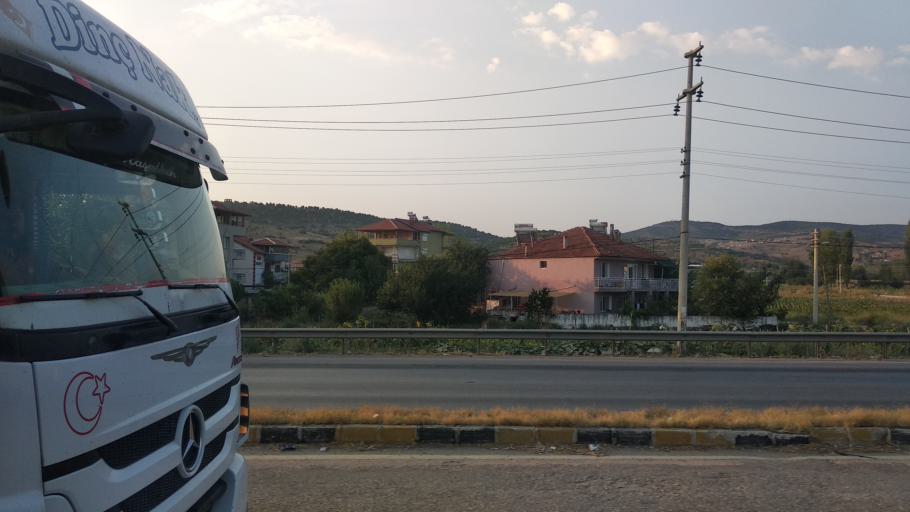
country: TR
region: Manisa
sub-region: Kula
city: Kula
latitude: 38.5427
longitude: 28.6571
